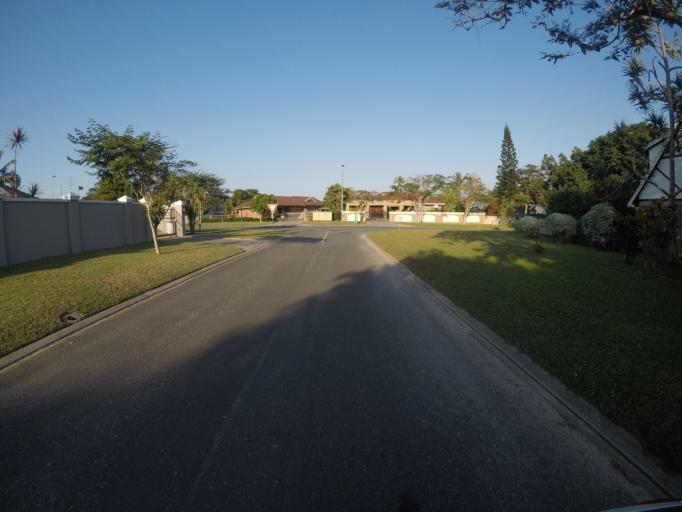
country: ZA
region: KwaZulu-Natal
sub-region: uThungulu District Municipality
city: Richards Bay
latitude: -28.7731
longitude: 32.1150
